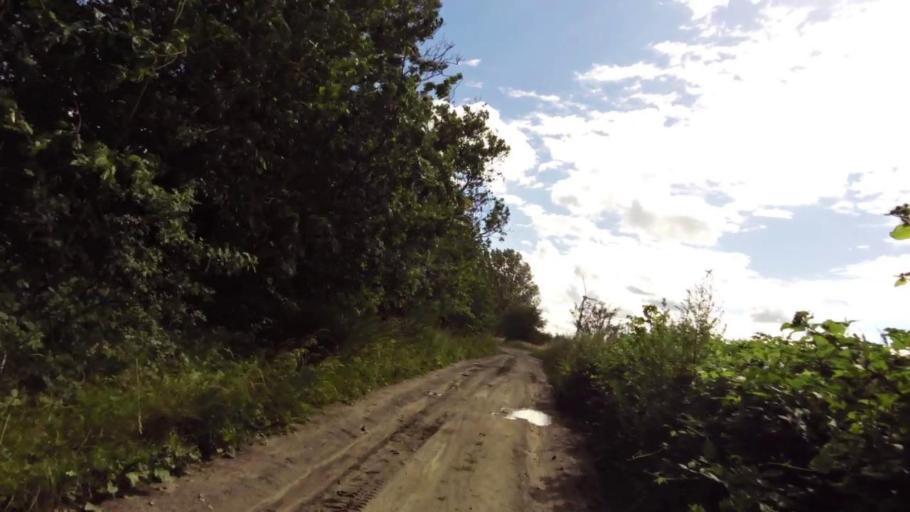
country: PL
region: West Pomeranian Voivodeship
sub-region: Powiat slawienski
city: Slawno
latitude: 54.5119
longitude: 16.7067
